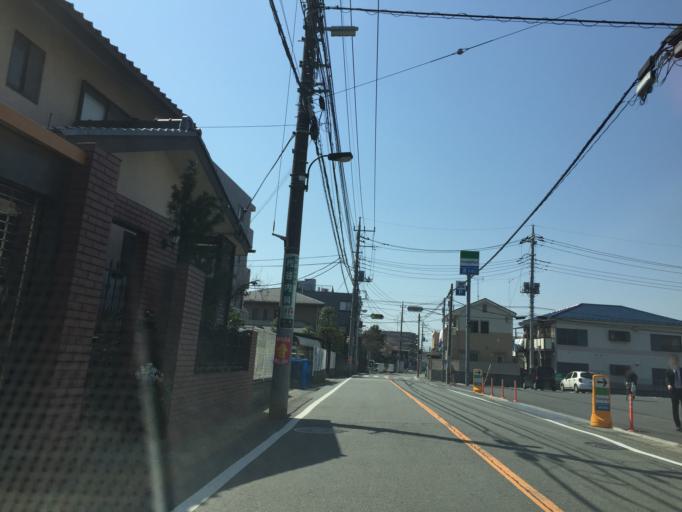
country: JP
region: Saitama
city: Yono
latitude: 35.8536
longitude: 139.6309
